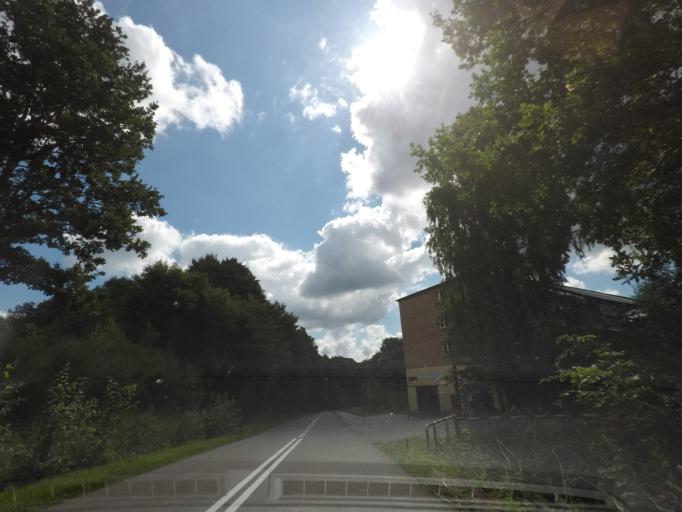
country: PL
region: Pomeranian Voivodeship
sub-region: Powiat wejherowski
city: Leczyce
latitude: 54.5979
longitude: 17.8463
